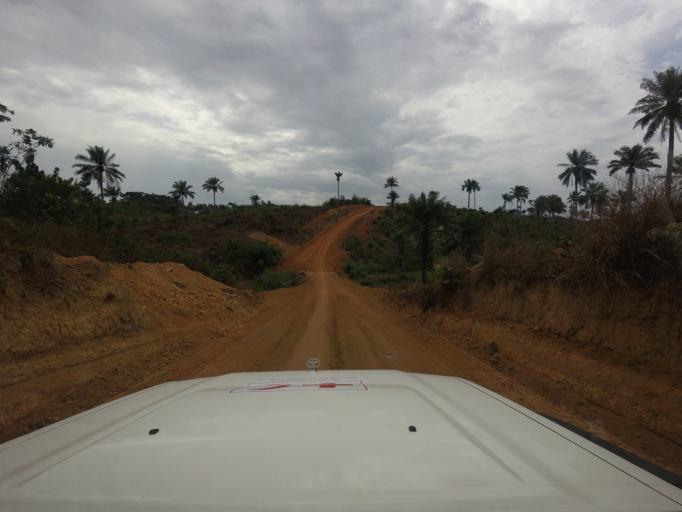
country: SL
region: Eastern Province
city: Buedu
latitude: 8.2498
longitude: -10.2250
